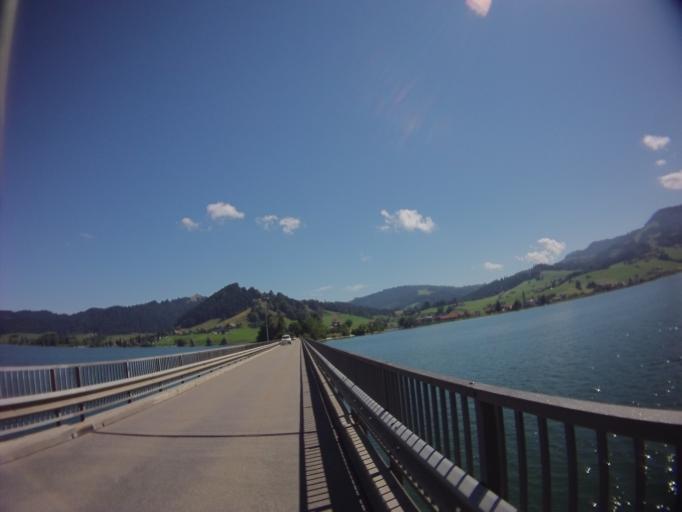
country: CH
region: Schwyz
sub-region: Bezirk Einsiedeln
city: Einsiedeln
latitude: 47.1310
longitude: 8.7810
